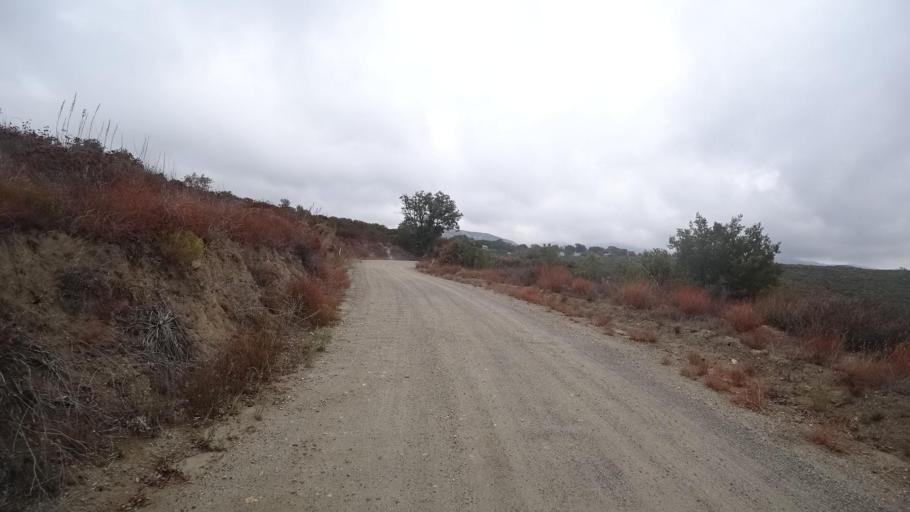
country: US
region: California
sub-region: San Diego County
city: Julian
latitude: 32.9842
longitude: -116.6679
